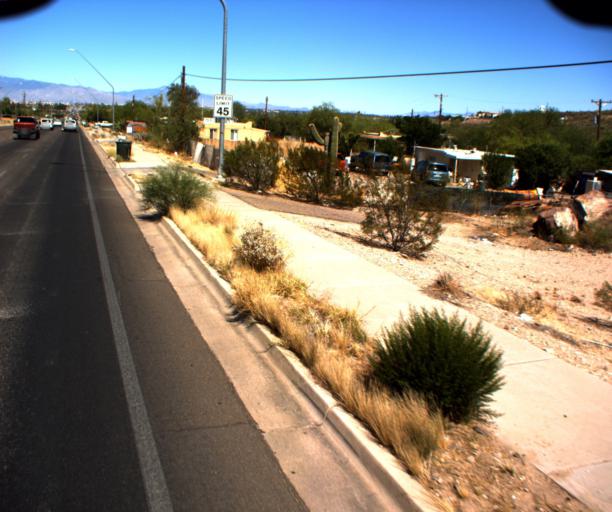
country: US
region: Arizona
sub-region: Pima County
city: Drexel Heights
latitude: 32.1778
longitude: -111.0108
